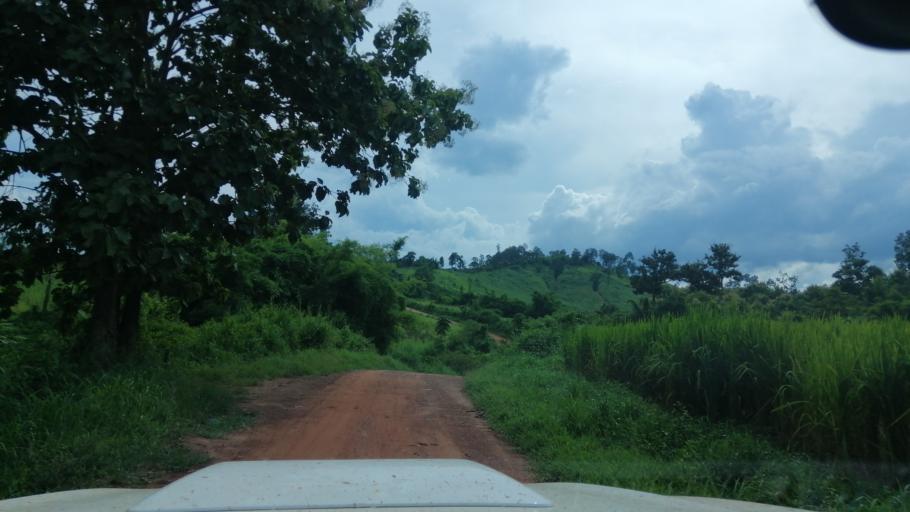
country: TH
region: Nan
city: Mae Charim
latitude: 18.7881
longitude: 101.3250
